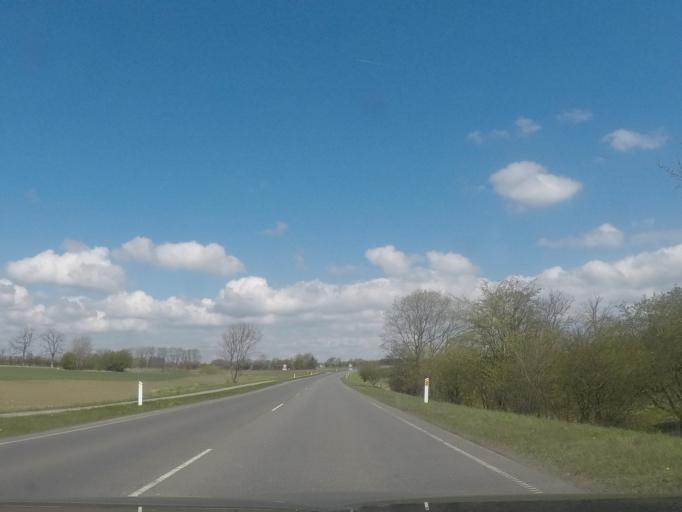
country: DK
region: South Denmark
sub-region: Assens Kommune
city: Vissenbjerg
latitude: 55.3842
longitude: 10.1080
